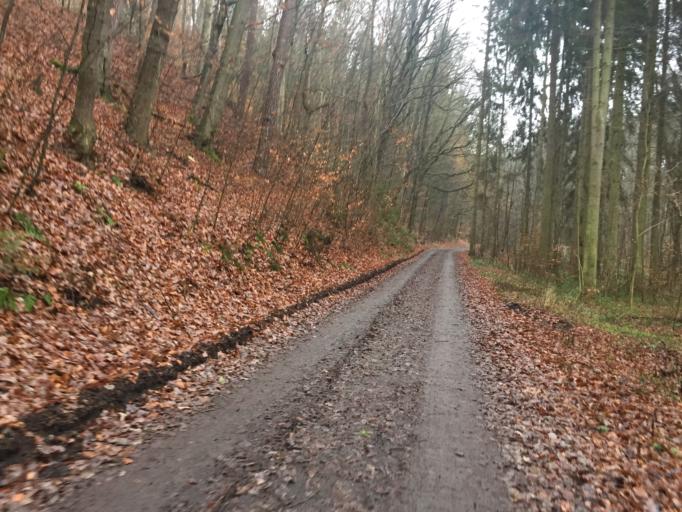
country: DE
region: Thuringia
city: Tissa
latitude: 50.8570
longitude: 11.7428
